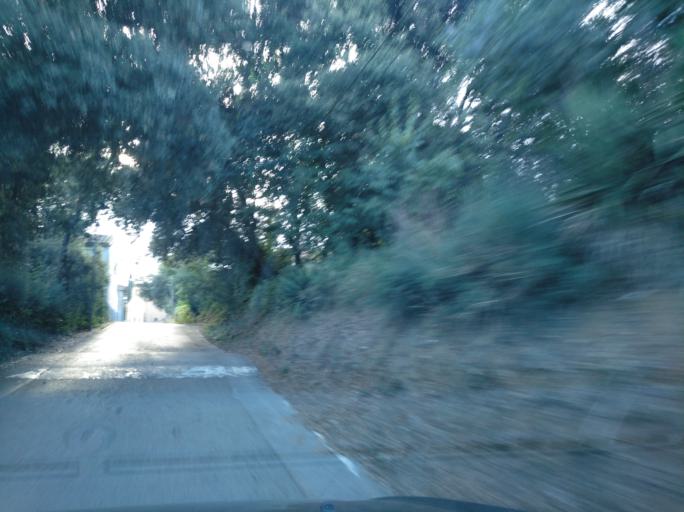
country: ES
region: Catalonia
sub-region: Provincia de Girona
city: Aiguaviva
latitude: 41.9416
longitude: 2.7739
